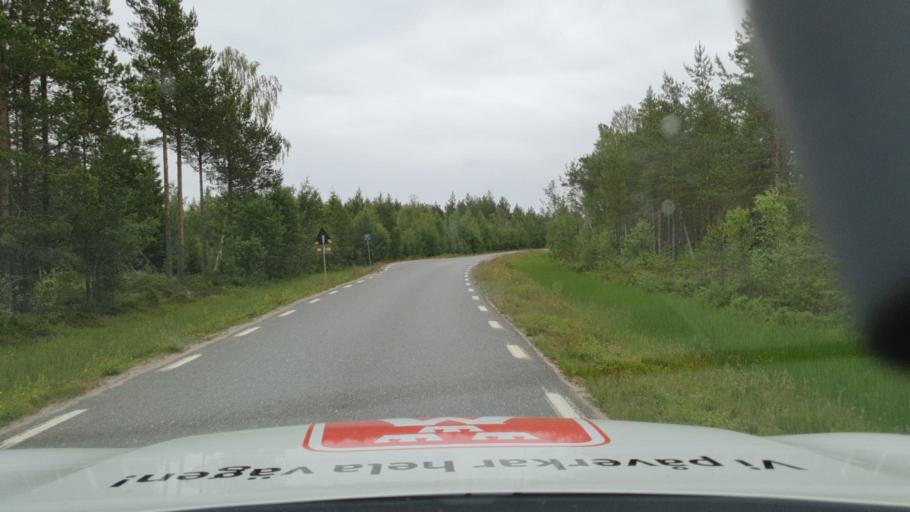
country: SE
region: Vaesterbotten
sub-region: Nordmalings Kommun
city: Nordmaling
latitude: 63.4330
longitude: 19.4831
